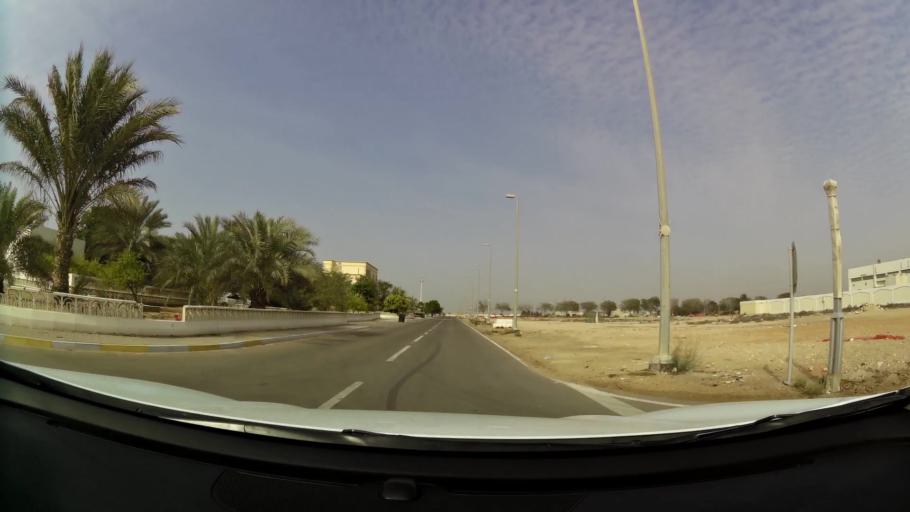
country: AE
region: Abu Dhabi
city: Abu Dhabi
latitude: 24.6131
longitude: 54.7047
